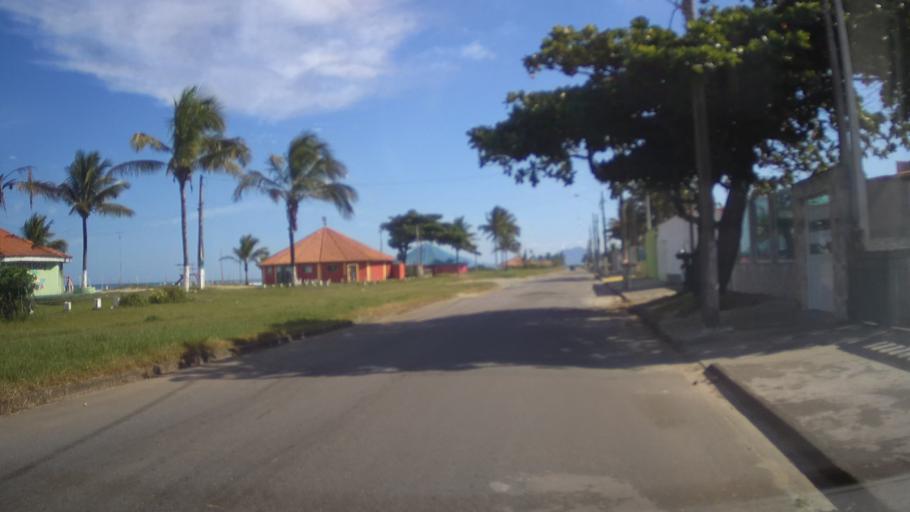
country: BR
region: Sao Paulo
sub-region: Itanhaem
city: Itanhaem
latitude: -24.2166
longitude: -46.8446
